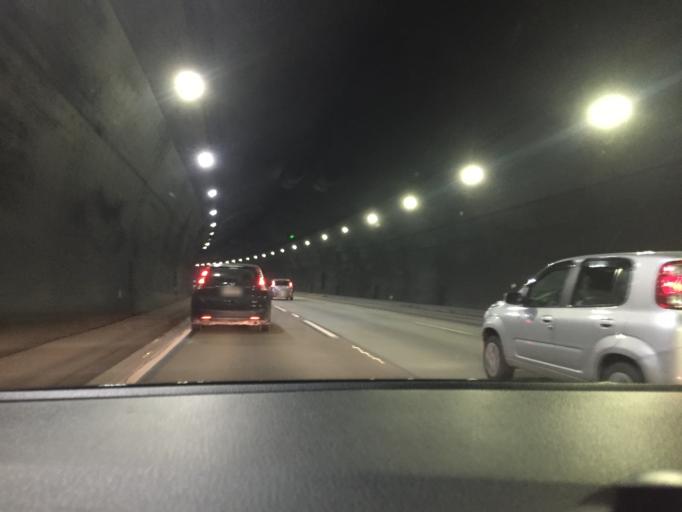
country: BR
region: Sao Paulo
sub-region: Cubatao
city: Cubatao
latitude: -23.8884
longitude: -46.5023
